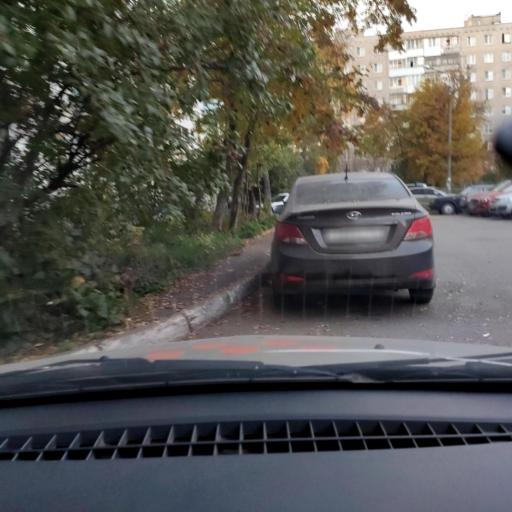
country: RU
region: Bashkortostan
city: Ufa
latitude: 54.7843
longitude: 56.1253
